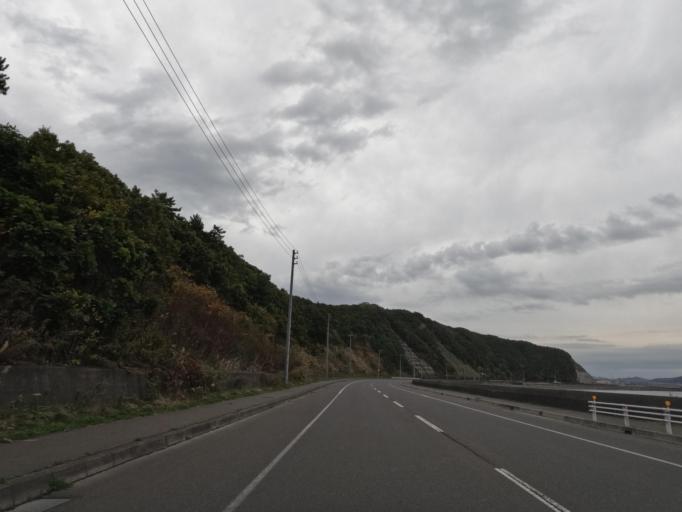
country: JP
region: Hokkaido
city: Muroran
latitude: 42.3766
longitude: 140.9100
